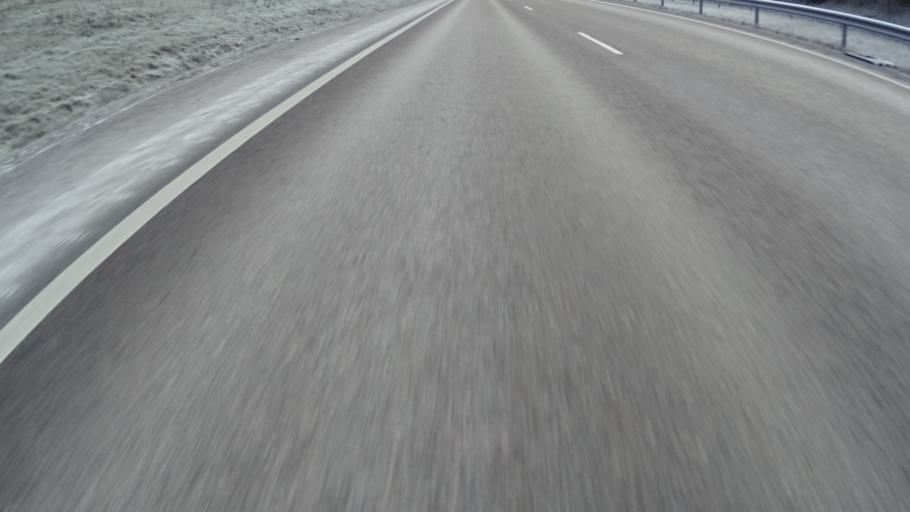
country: FI
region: Uusimaa
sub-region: Helsinki
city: Kilo
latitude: 60.3225
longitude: 24.8305
